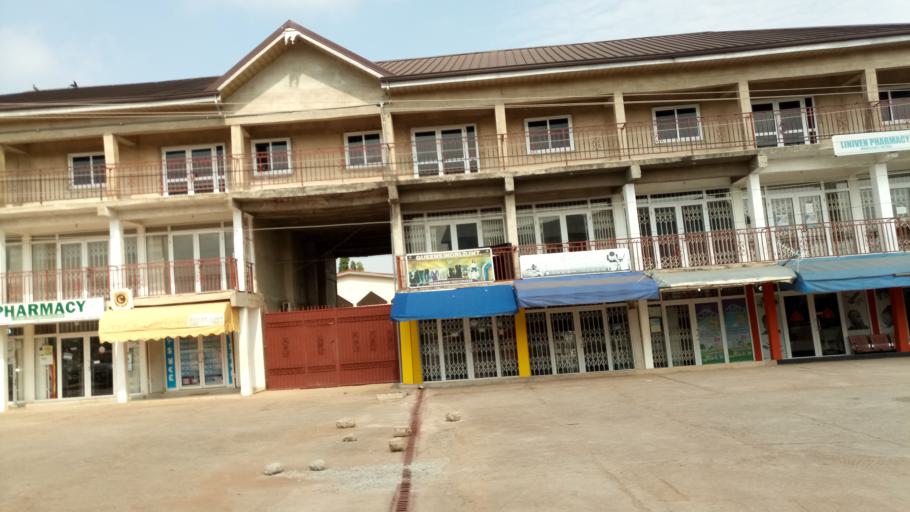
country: GH
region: Greater Accra
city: Medina Estates
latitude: 5.6760
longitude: -0.1914
